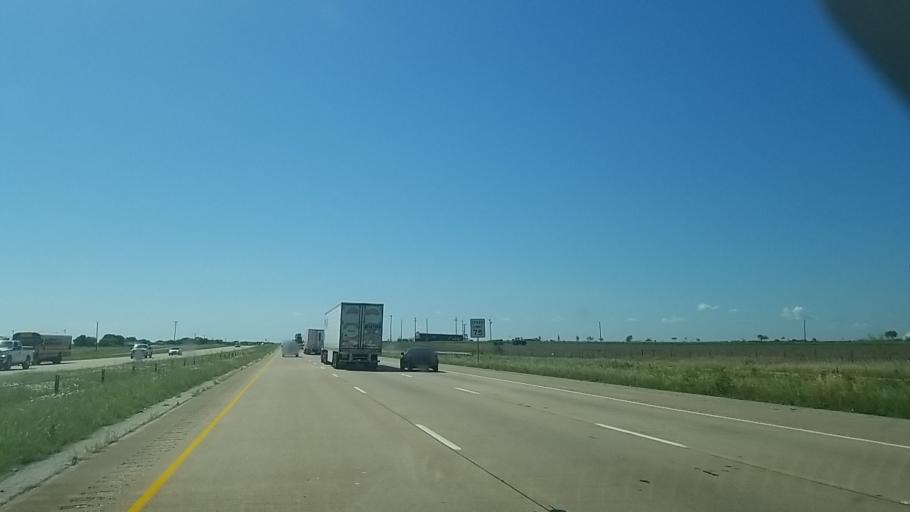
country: US
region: Texas
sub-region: Ellis County
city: Ennis
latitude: 32.2760
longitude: -96.5221
